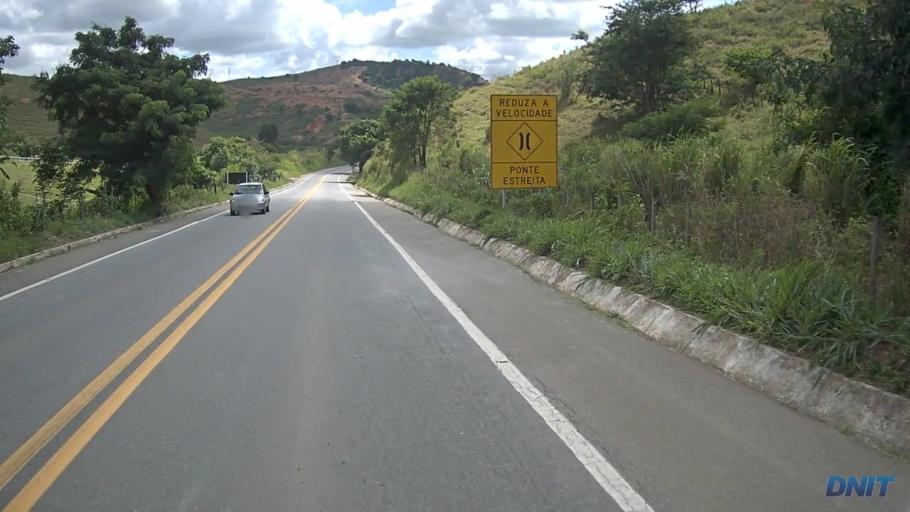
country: BR
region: Minas Gerais
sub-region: Governador Valadares
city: Governador Valadares
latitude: -18.9506
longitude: -42.0708
